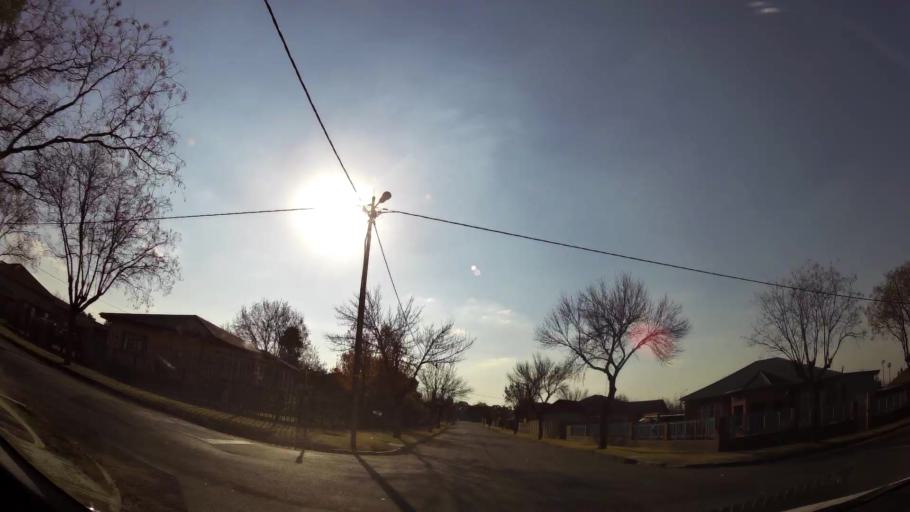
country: ZA
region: Gauteng
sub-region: Ekurhuleni Metropolitan Municipality
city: Brakpan
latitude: -26.2330
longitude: 28.3603
